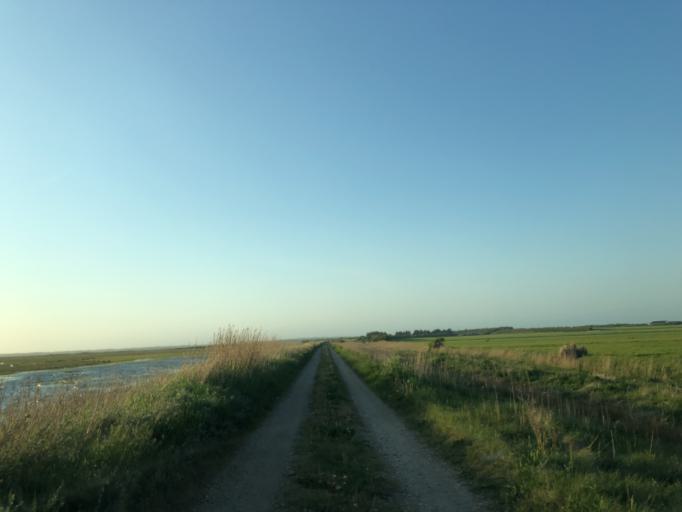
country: DK
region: Central Jutland
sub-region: Ringkobing-Skjern Kommune
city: Ringkobing
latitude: 56.2200
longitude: 8.1656
